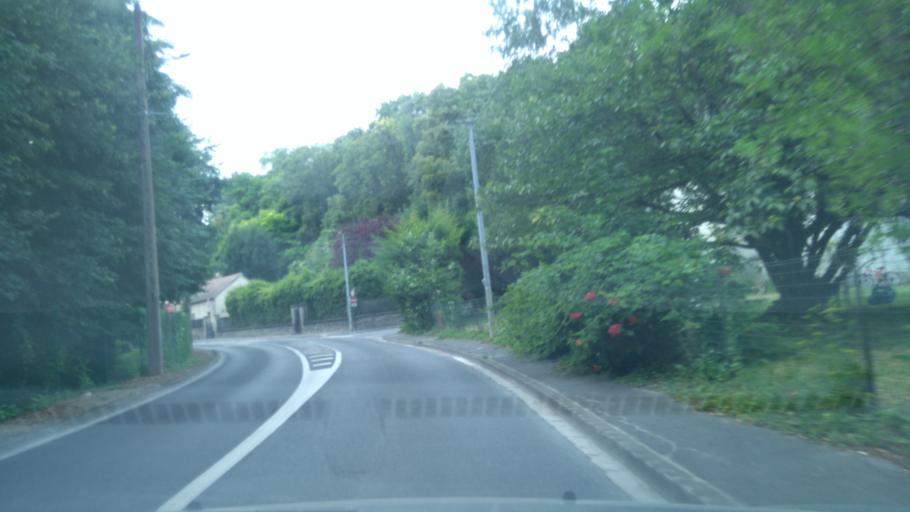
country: FR
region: Picardie
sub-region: Departement de l'Oise
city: Gouvieux
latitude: 49.1989
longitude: 2.4205
